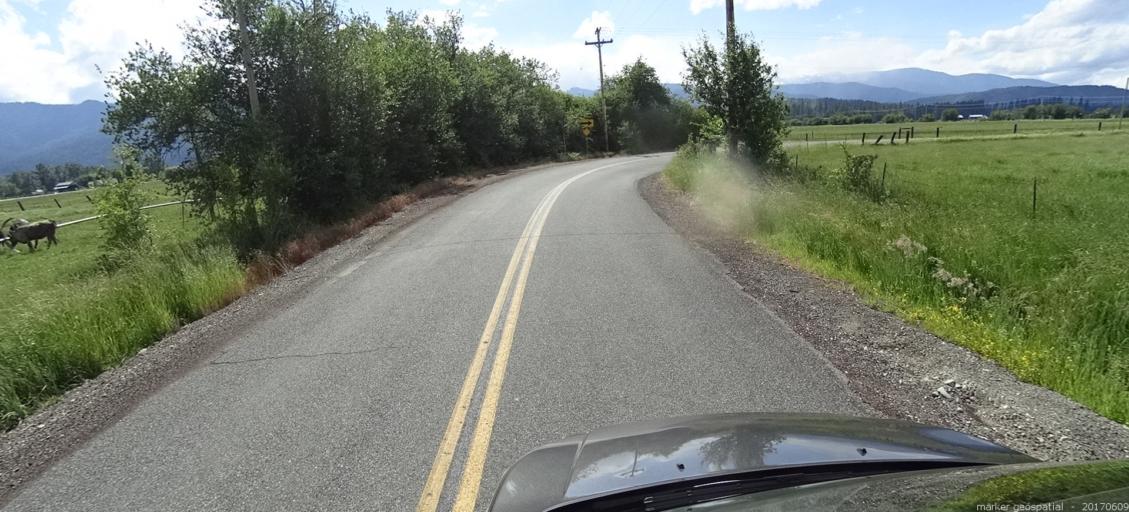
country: US
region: California
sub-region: Siskiyou County
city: Yreka
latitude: 41.5130
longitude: -122.8875
